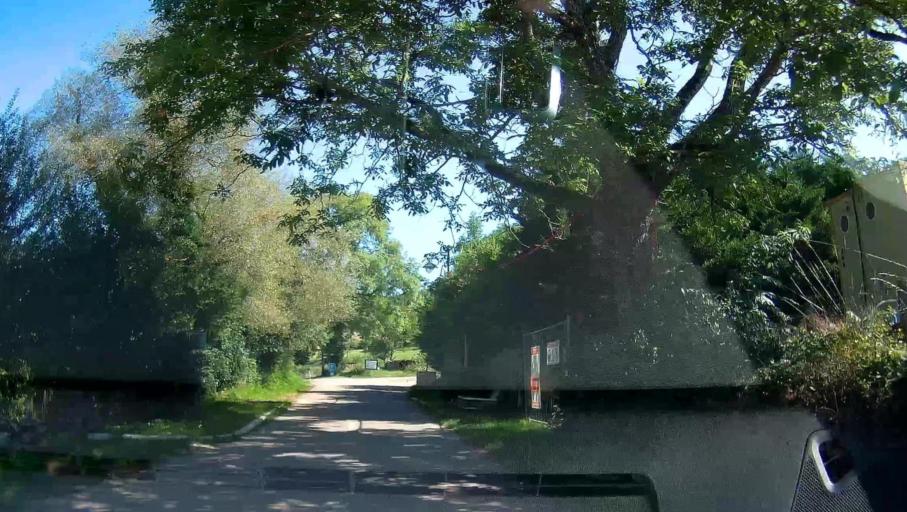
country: FR
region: Bourgogne
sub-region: Departement de la Cote-d'Or
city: Nolay
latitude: 46.9776
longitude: 4.6449
